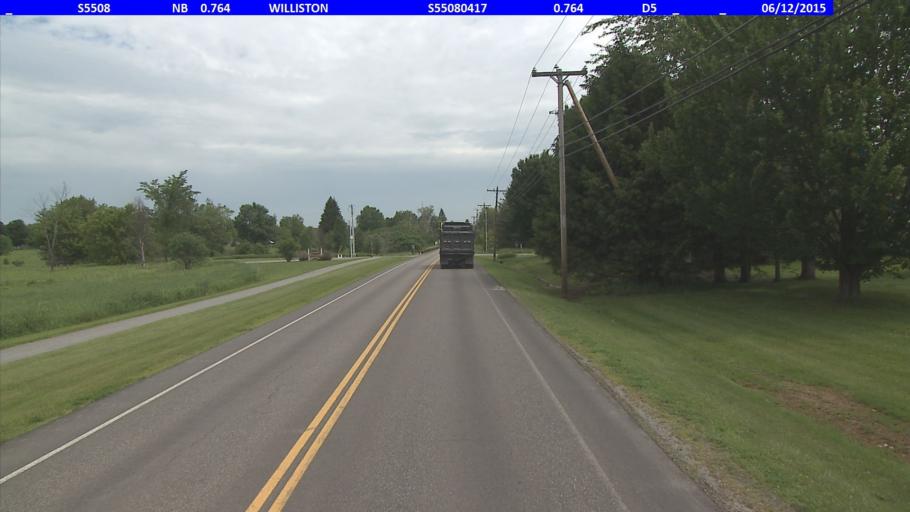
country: US
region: Vermont
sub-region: Chittenden County
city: Williston
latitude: 44.4475
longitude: -73.0620
